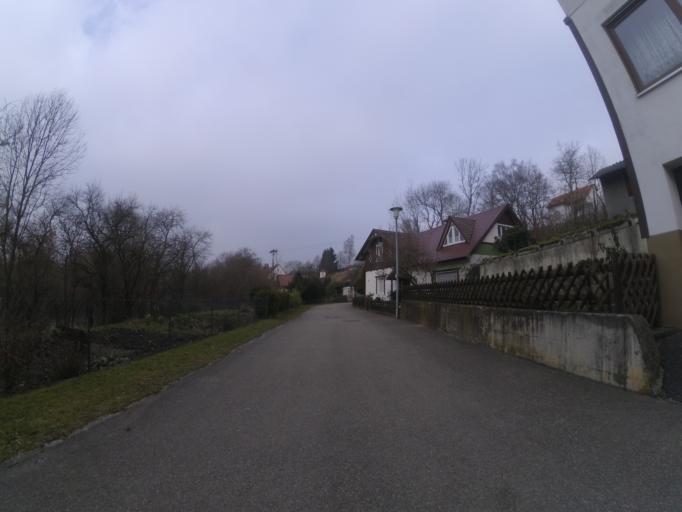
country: DE
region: Baden-Wuerttemberg
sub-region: Tuebingen Region
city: Munderkingen
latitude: 48.2386
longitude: 9.6398
